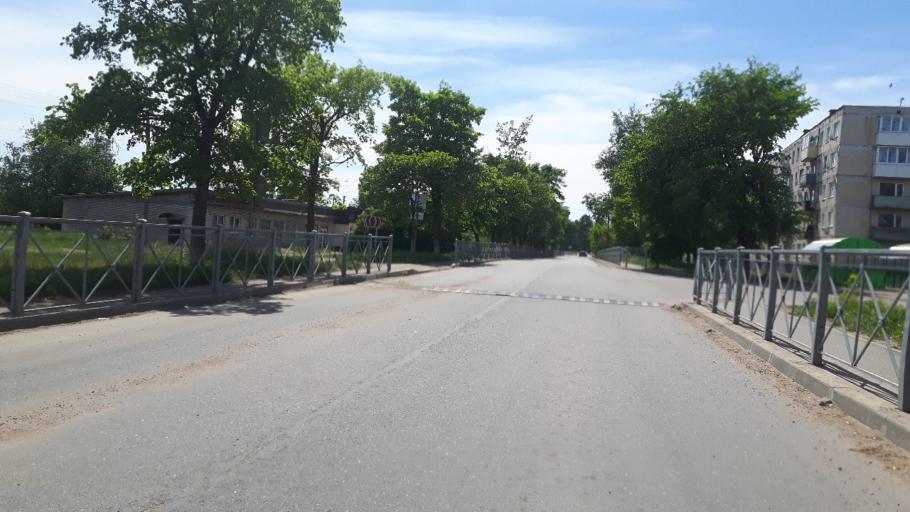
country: RU
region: Leningrad
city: Ust'-Luga
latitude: 59.5815
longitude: 28.1800
